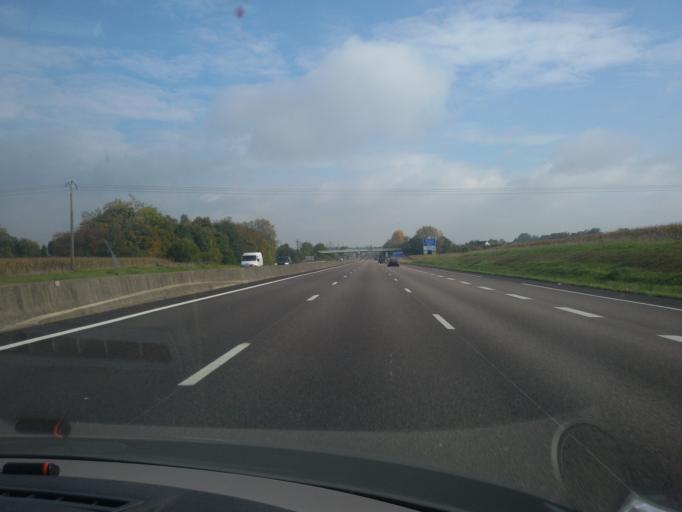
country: FR
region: Haute-Normandie
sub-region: Departement de l'Eure
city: Bourg-Achard
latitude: 49.3635
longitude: 0.8390
